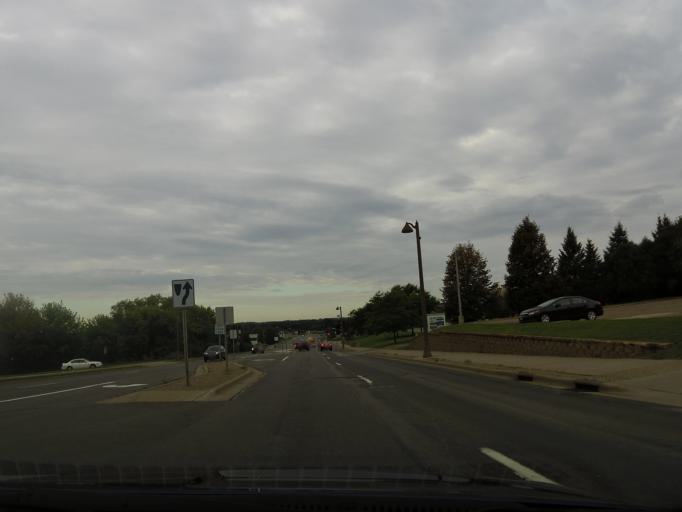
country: US
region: Minnesota
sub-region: Washington County
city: Cottage Grove
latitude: 44.8336
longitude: -92.9550
